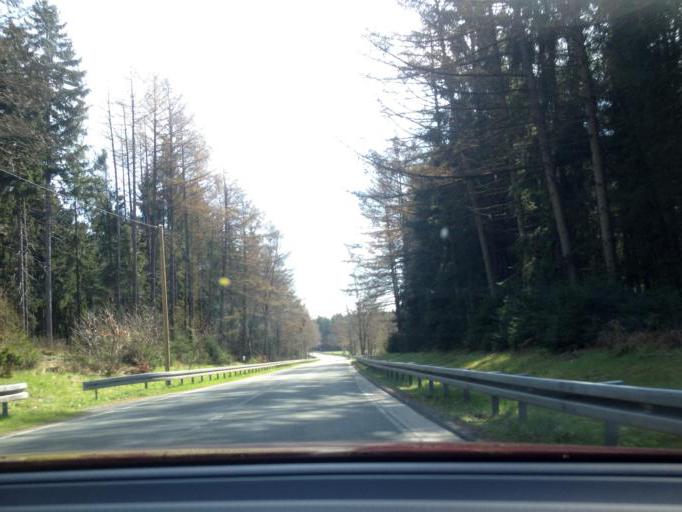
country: DE
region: Bavaria
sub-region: Upper Franconia
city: Oberhaid
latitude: 50.0967
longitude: 11.8237
